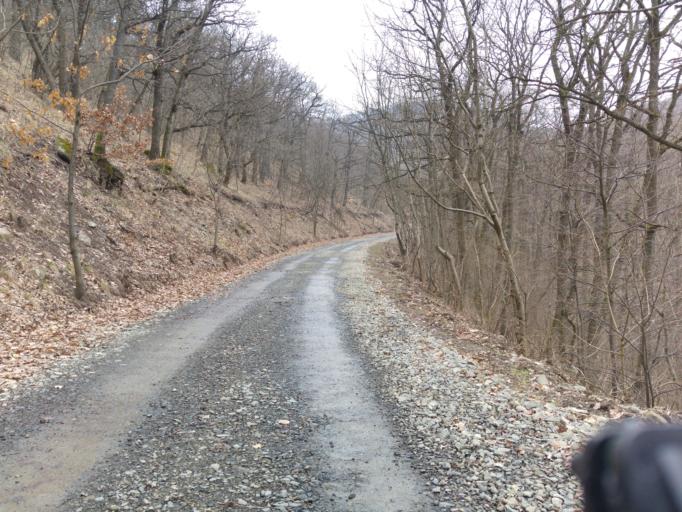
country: HU
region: Pest
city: Dunabogdany
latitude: 47.7511
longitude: 19.0270
